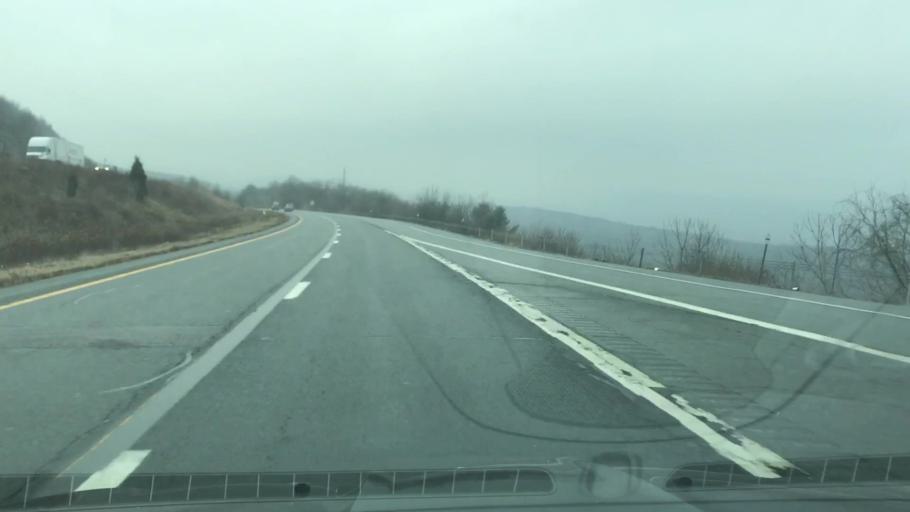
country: US
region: New York
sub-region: Orange County
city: Port Jervis
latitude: 41.3730
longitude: -74.6402
